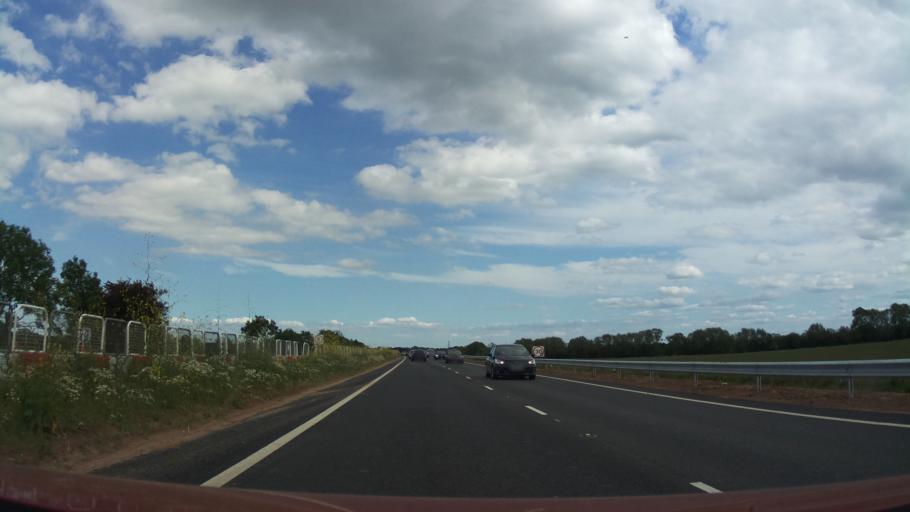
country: GB
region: England
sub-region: Worcestershire
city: Worcester
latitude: 52.1667
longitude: -2.2384
